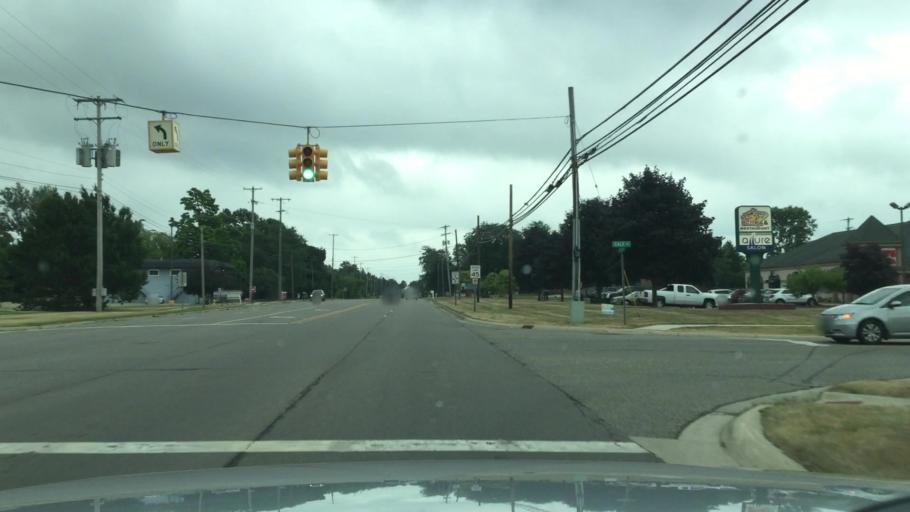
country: US
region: Michigan
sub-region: Genesee County
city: Davison
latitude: 43.0343
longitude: -83.5380
